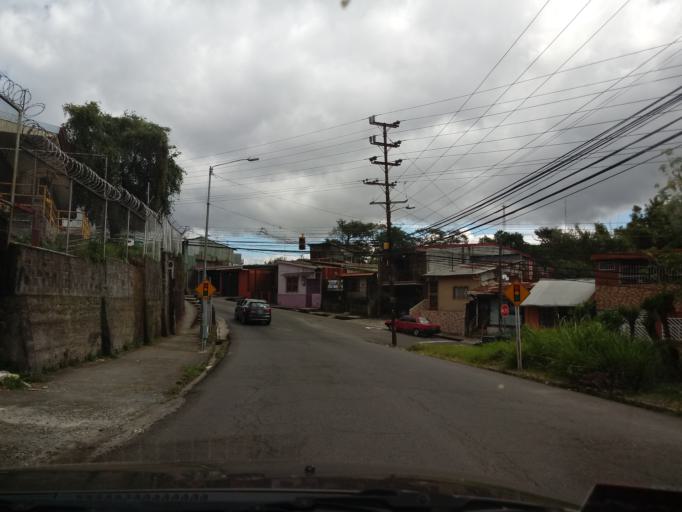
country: CR
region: San Jose
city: Calle Blancos
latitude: 9.9429
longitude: -84.0682
